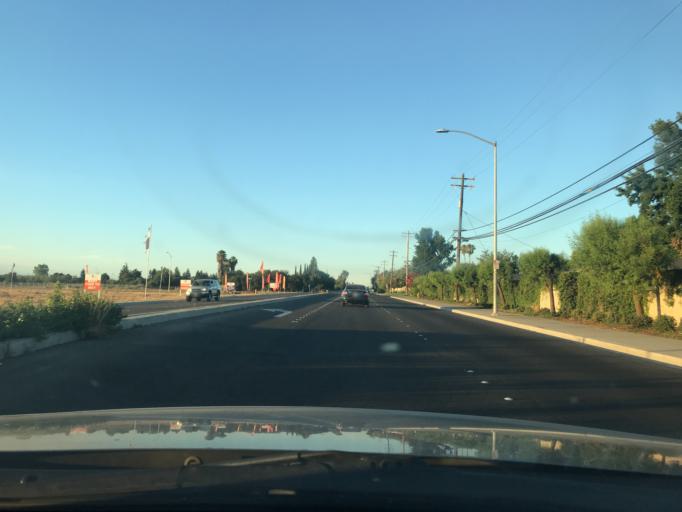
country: US
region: California
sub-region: Merced County
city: Atwater
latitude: 37.3569
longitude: -120.5767
